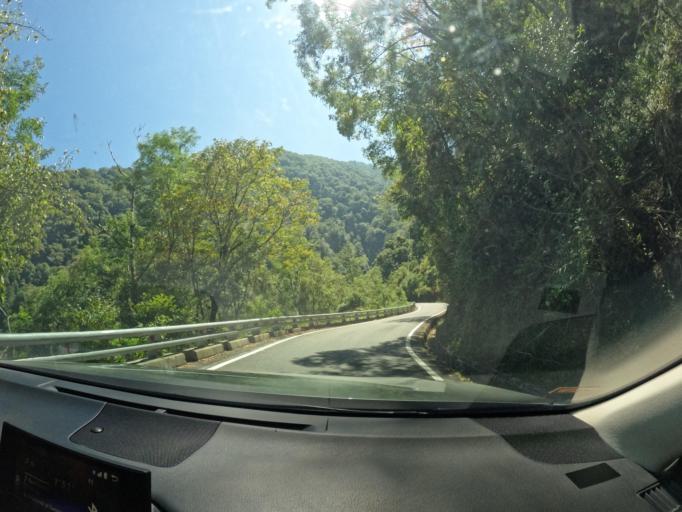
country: TW
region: Taiwan
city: Yujing
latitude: 23.2827
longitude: 120.8732
